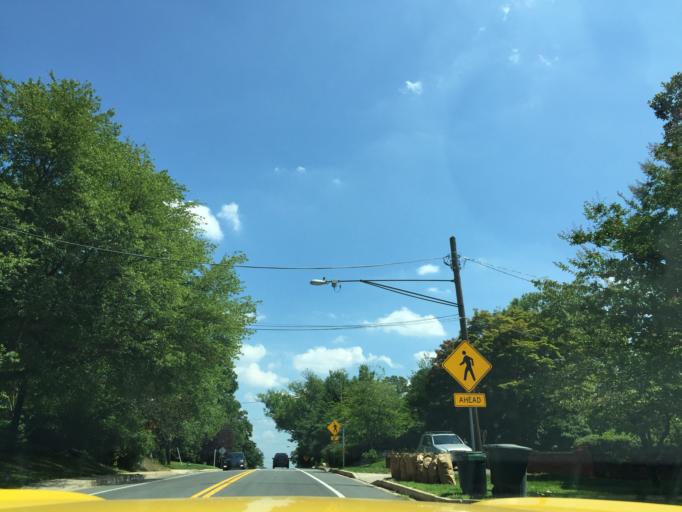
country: US
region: Maryland
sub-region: Montgomery County
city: Brookmont
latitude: 38.9655
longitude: -77.1238
